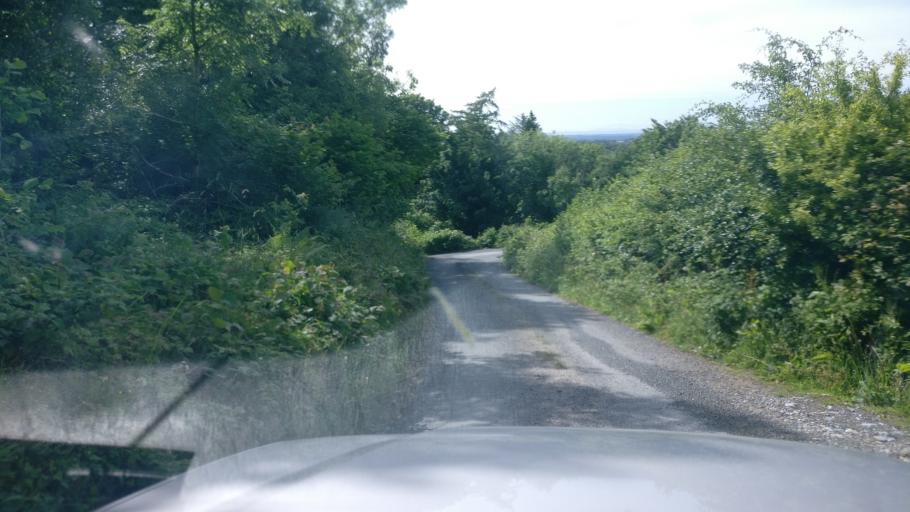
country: IE
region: Connaught
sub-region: County Galway
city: Gort
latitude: 53.0937
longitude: -8.6995
